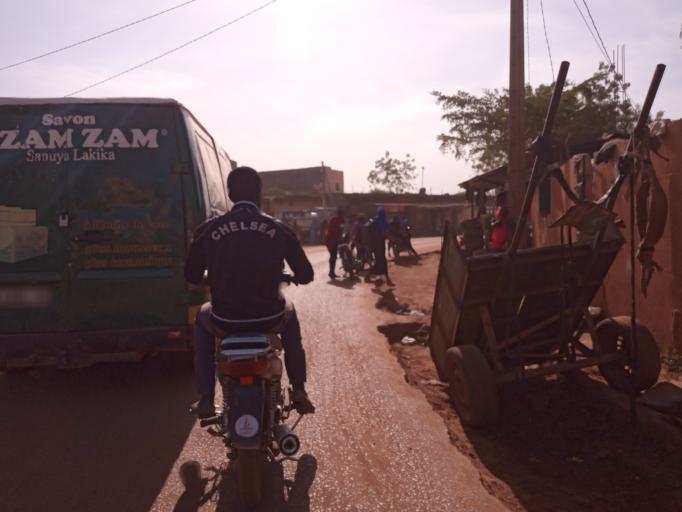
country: ML
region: Bamako
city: Bamako
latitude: 12.6205
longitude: -7.9558
